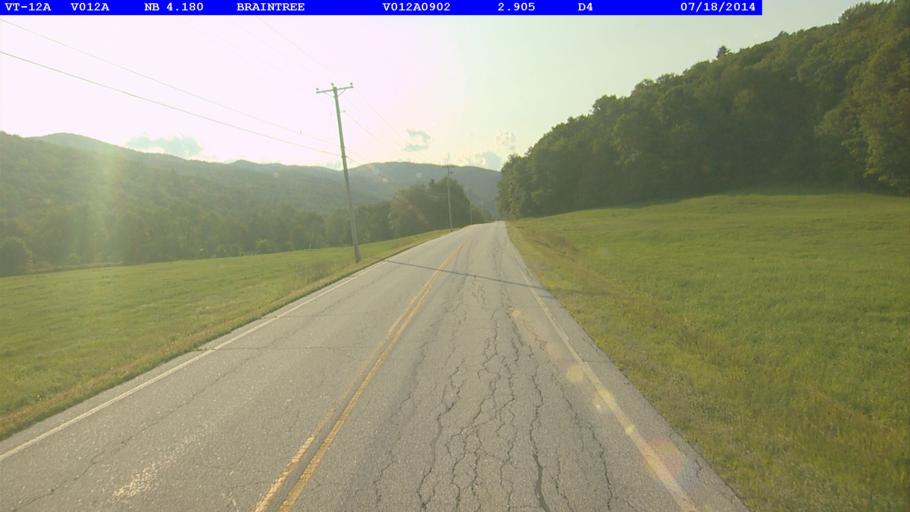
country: US
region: Vermont
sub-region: Orange County
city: Randolph
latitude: 43.9562
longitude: -72.7267
